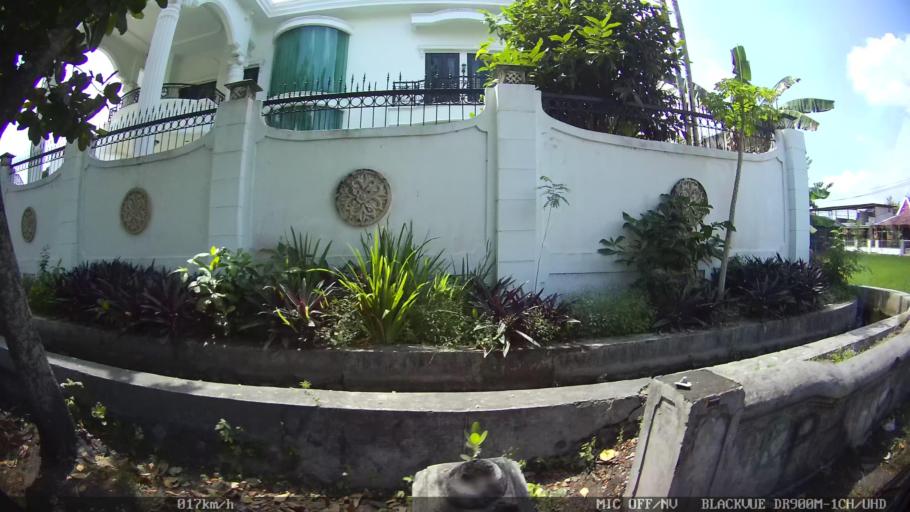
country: ID
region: Daerah Istimewa Yogyakarta
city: Yogyakarta
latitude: -7.8277
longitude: 110.3773
